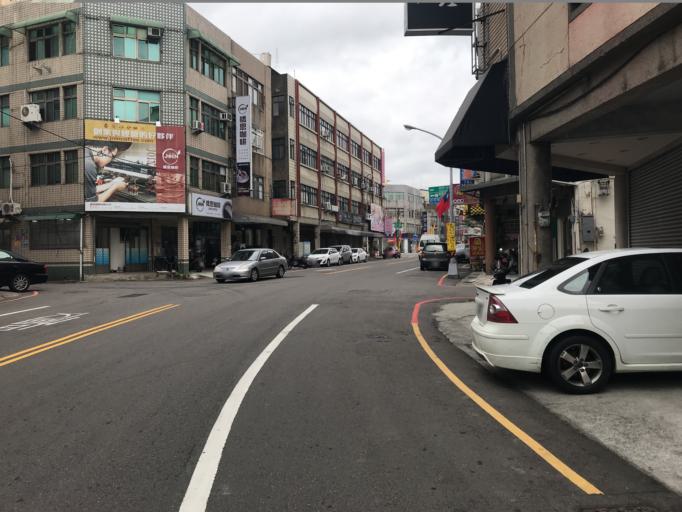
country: TW
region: Taiwan
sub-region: Miaoli
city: Miaoli
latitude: 24.5650
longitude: 120.8217
